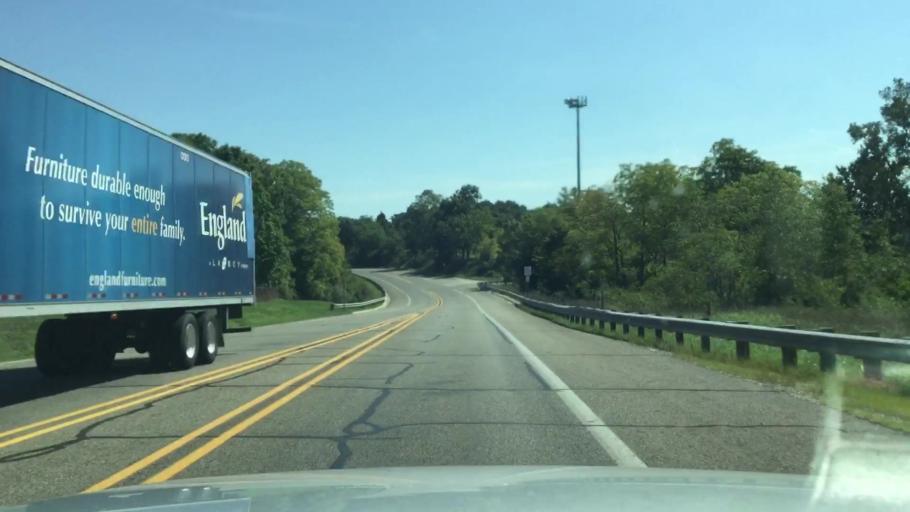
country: US
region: Michigan
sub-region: Jackson County
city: Brooklyn
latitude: 42.0580
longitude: -84.2402
